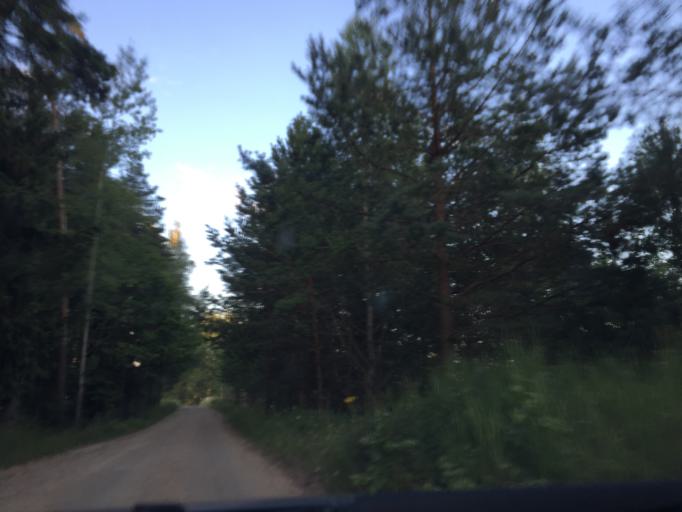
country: LV
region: Koknese
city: Koknese
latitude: 56.6212
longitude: 25.4893
